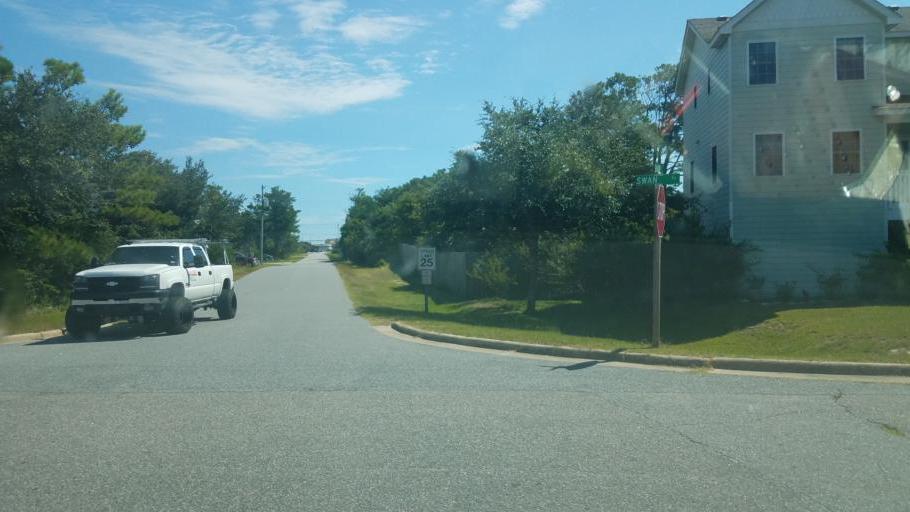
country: US
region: North Carolina
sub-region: Dare County
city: Kill Devil Hills
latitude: 36.0060
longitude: -75.6614
